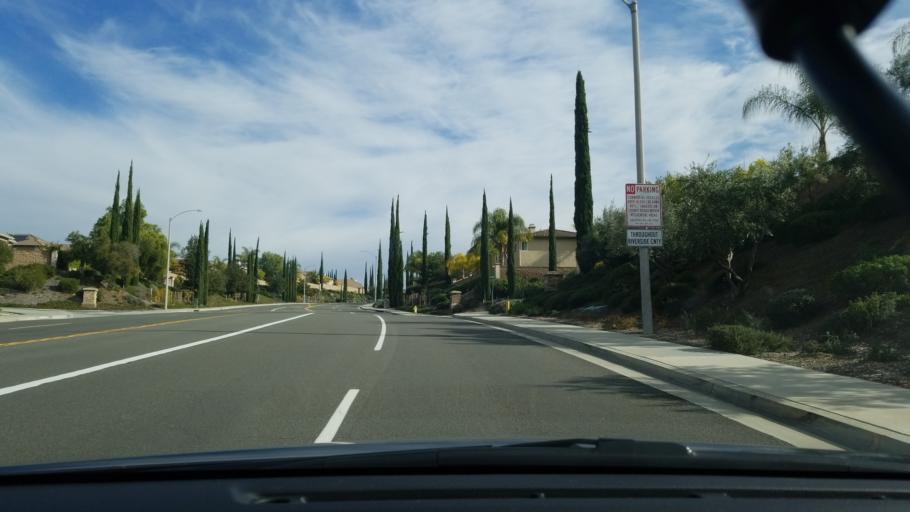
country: US
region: California
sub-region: Riverside County
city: Temecula
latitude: 33.4769
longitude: -117.0691
